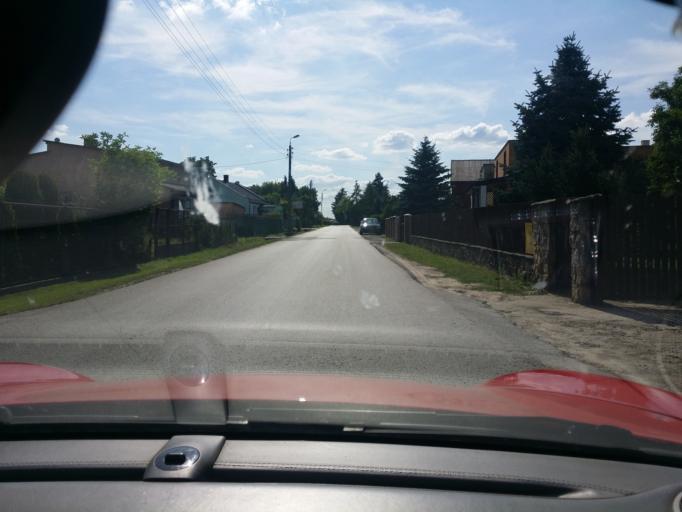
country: PL
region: Masovian Voivodeship
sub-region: Powiat radomski
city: Trablice
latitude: 51.3472
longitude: 21.0969
